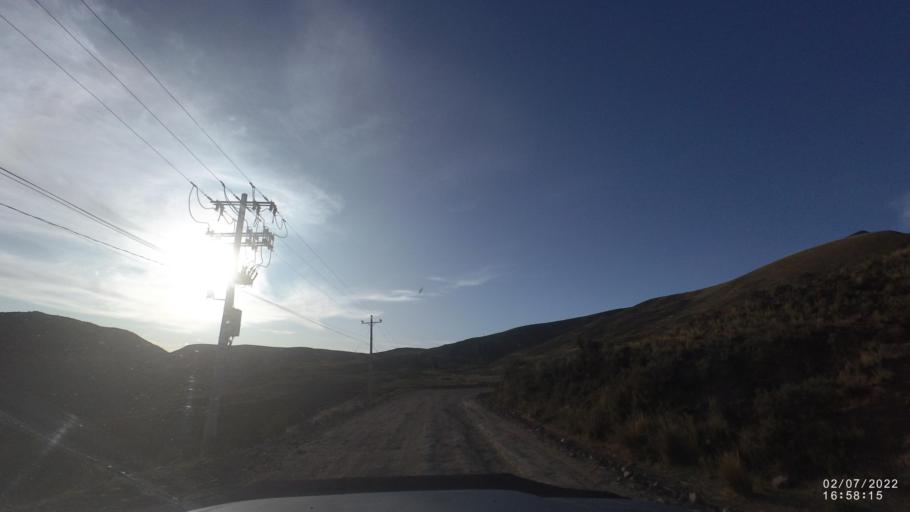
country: BO
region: Cochabamba
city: Irpa Irpa
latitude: -17.9474
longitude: -66.5478
